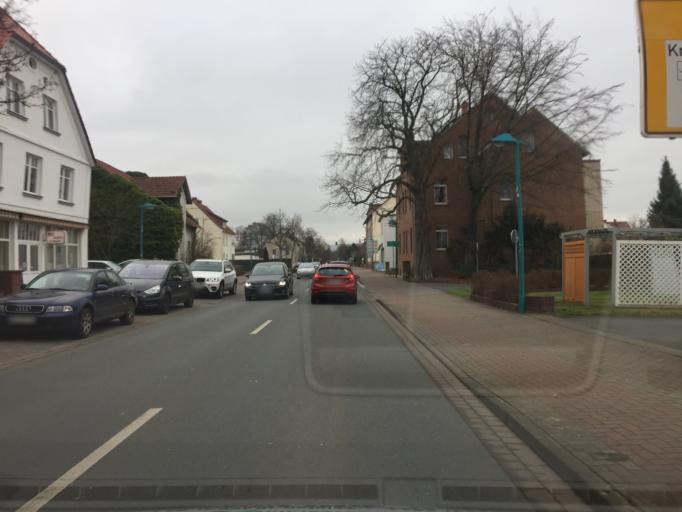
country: DE
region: Lower Saxony
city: Stadthagen
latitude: 52.3304
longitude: 9.1921
